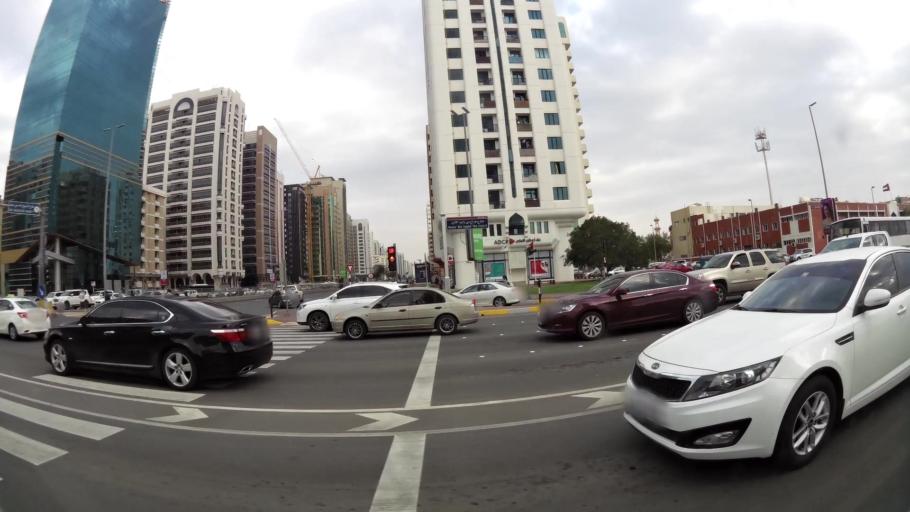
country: AE
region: Abu Dhabi
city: Abu Dhabi
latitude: 24.4700
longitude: 54.3704
